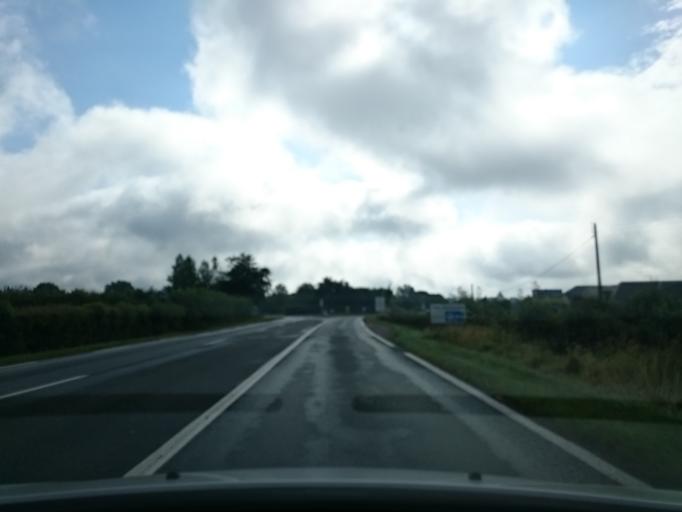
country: FR
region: Lower Normandy
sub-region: Departement du Calvados
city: Saint-Desir
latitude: 49.1374
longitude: 0.1699
